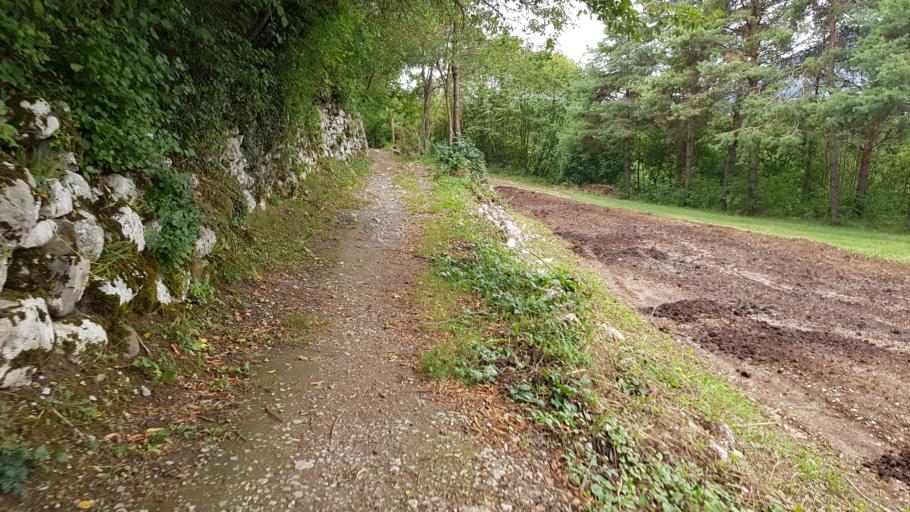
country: IT
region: Trentino-Alto Adige
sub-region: Provincia di Trento
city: Cavedine
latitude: 46.0071
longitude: 10.9724
